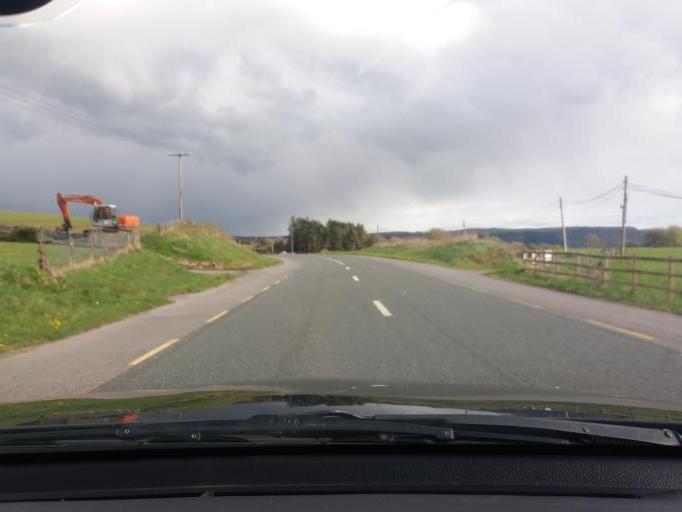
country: IE
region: Connaught
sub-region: County Leitrim
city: Manorhamilton
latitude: 54.3169
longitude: -8.1943
